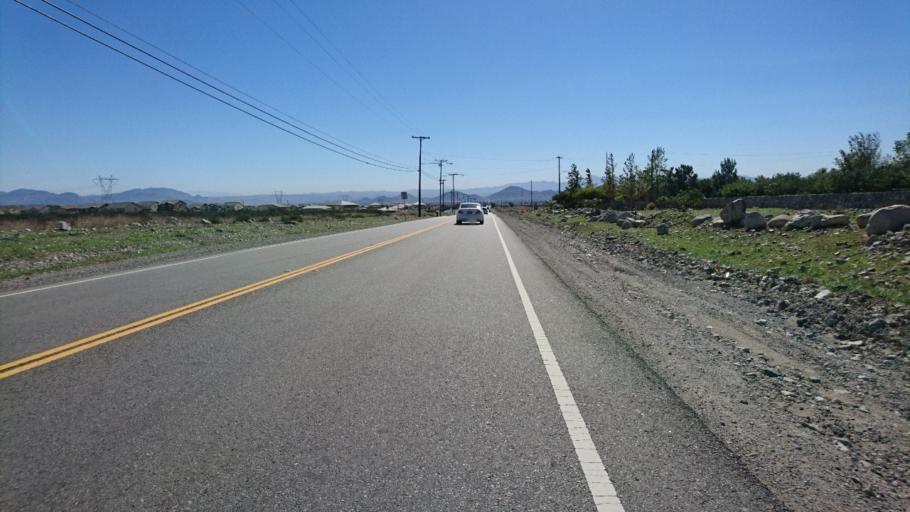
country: US
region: California
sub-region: San Bernardino County
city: Fontana
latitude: 34.1749
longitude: -117.4363
